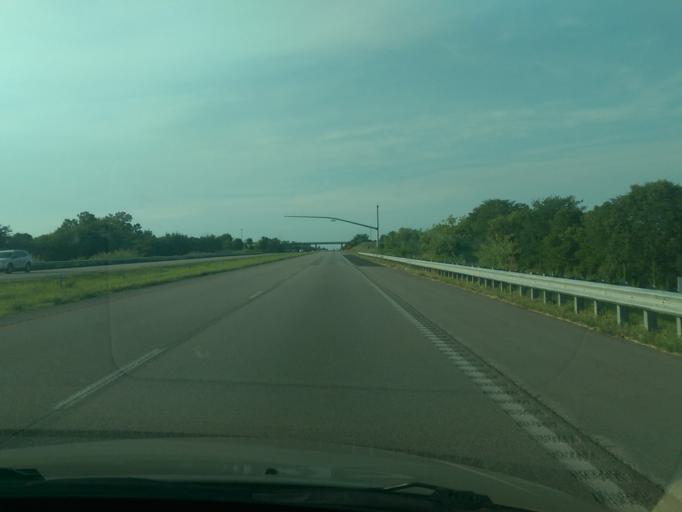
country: US
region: Missouri
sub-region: Platte County
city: Platte City
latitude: 39.4150
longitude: -94.7897
